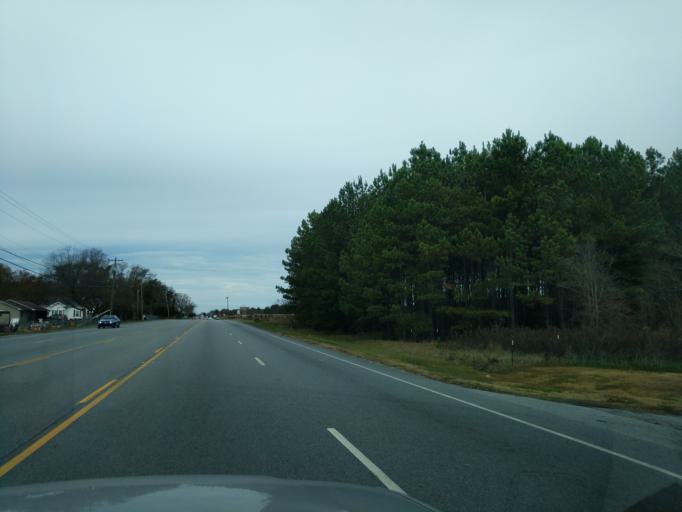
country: US
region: South Carolina
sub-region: Anderson County
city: Northlake
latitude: 34.5884
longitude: -82.7435
